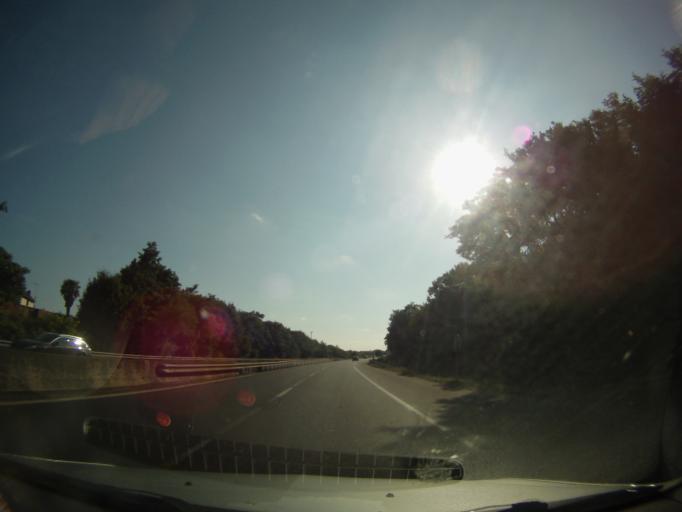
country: FR
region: Pays de la Loire
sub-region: Departement de la Loire-Atlantique
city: La Chapelle-sur-Erdre
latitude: 47.2765
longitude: -1.5213
